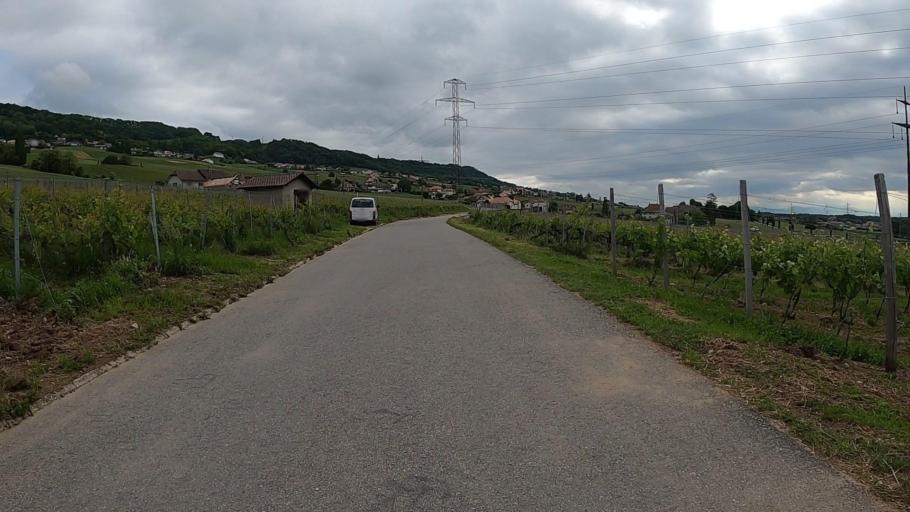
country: CH
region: Vaud
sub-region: Nyon District
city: Rolle
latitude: 46.4657
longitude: 6.3260
